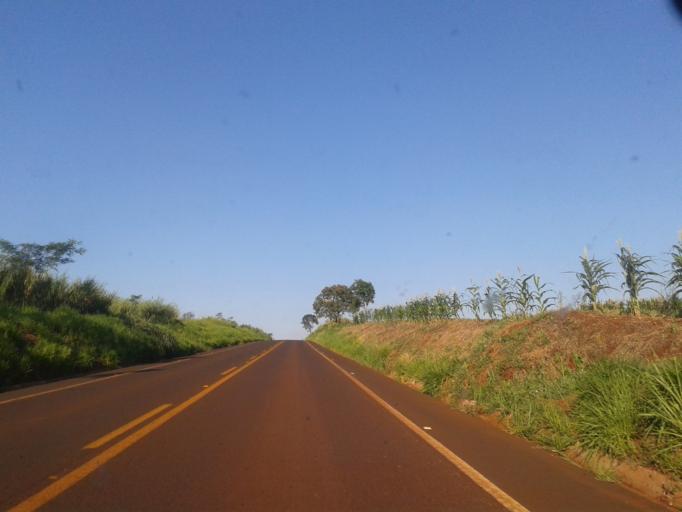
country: BR
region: Minas Gerais
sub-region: Capinopolis
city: Capinopolis
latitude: -18.7118
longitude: -49.7349
